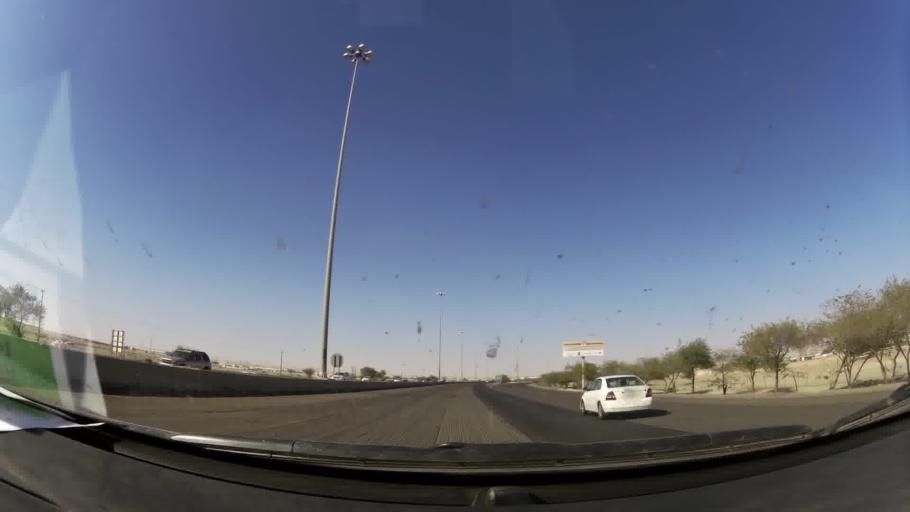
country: KW
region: Muhafazat al Jahra'
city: Al Jahra'
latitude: 29.3283
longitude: 47.6347
